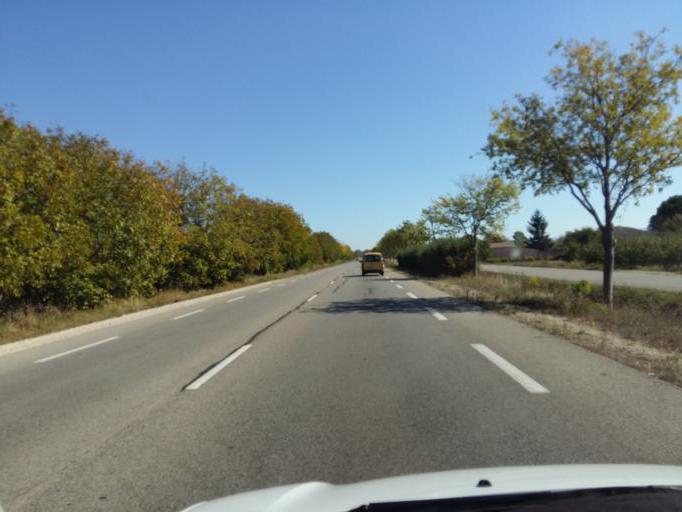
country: FR
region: Provence-Alpes-Cote d'Azur
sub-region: Departement du Vaucluse
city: Cadenet
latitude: 43.7330
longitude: 5.3551
